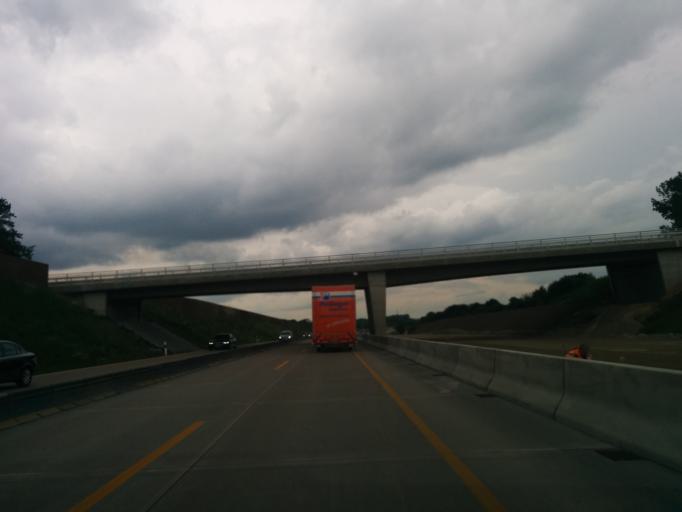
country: DE
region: Bavaria
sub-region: Swabia
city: Rettenbach
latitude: 48.4330
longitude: 10.3437
